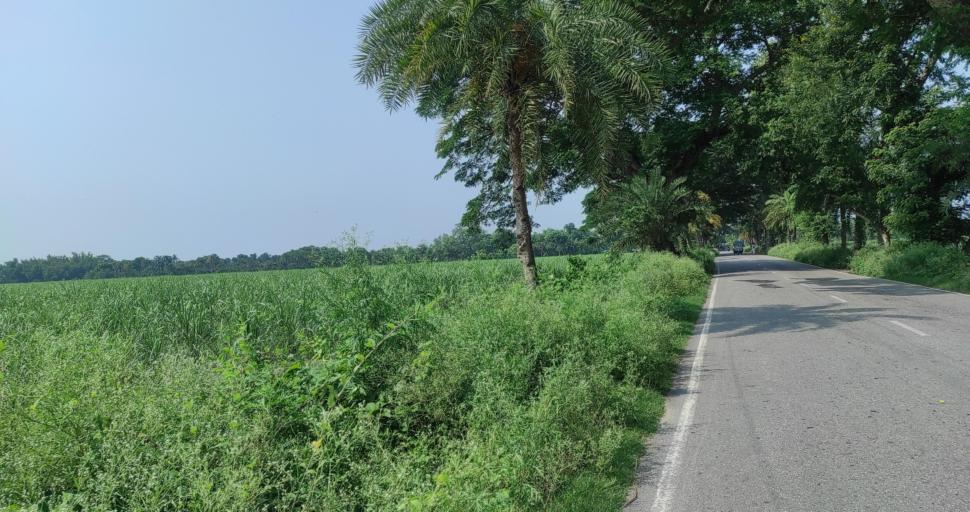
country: BD
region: Rajshahi
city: Ishurdi
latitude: 24.2645
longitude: 89.0506
